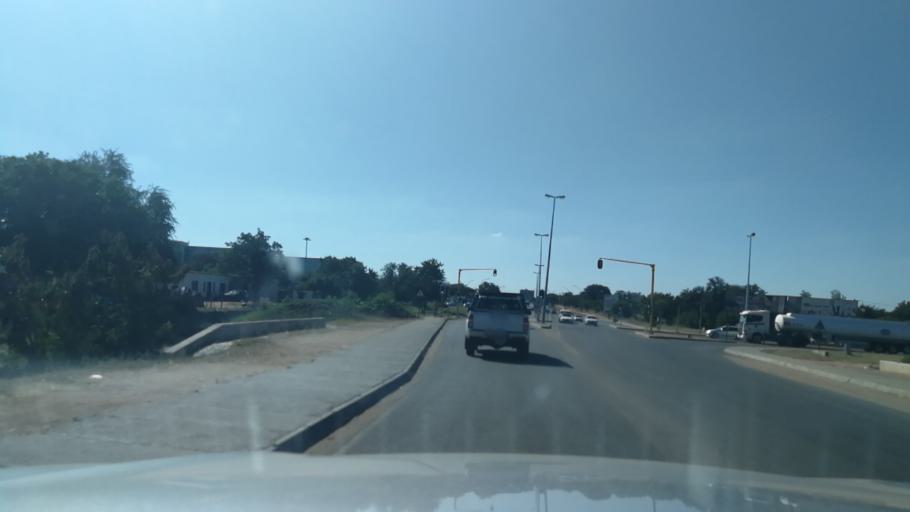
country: BW
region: South East
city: Gaborone
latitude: -24.6820
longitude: 25.9059
